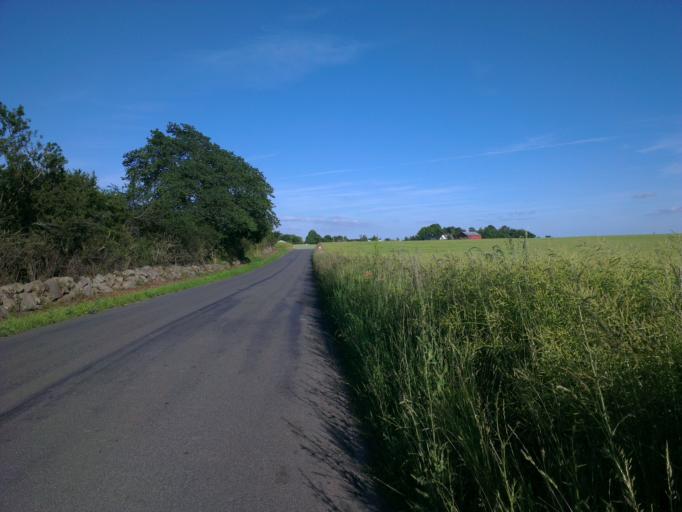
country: DK
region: Capital Region
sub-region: Frederikssund Kommune
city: Skibby
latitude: 55.7387
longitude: 12.0211
